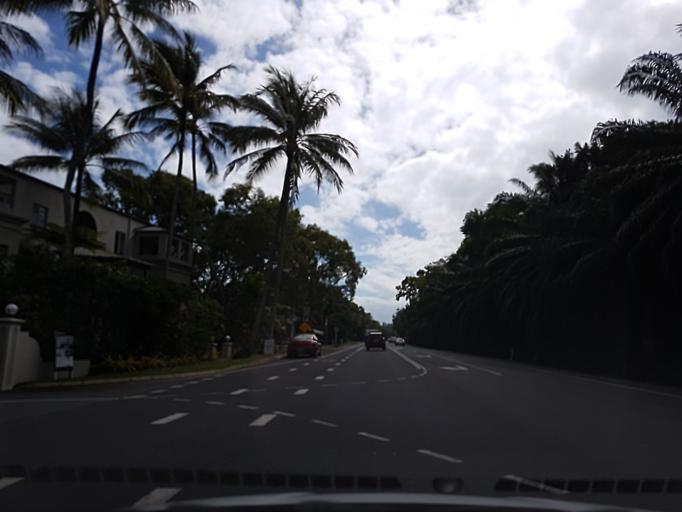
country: AU
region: Queensland
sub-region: Cairns
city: Port Douglas
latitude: -16.4999
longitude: 145.4633
